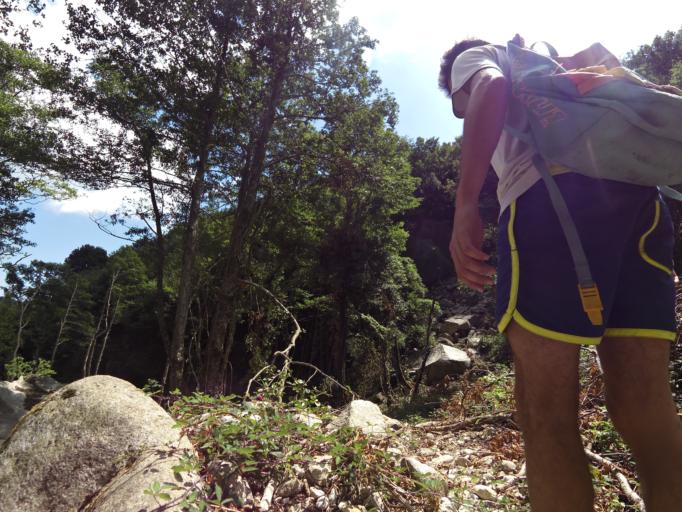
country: IT
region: Calabria
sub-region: Provincia di Vibo-Valentia
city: Nardodipace
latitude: 38.5029
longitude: 16.3925
